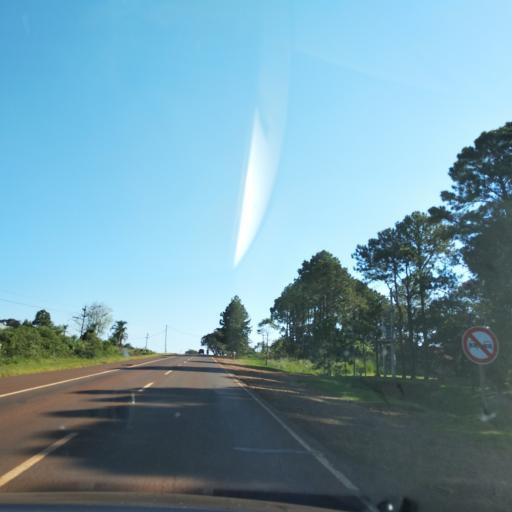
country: AR
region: Misiones
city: Jardin America
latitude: -27.0587
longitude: -55.2577
